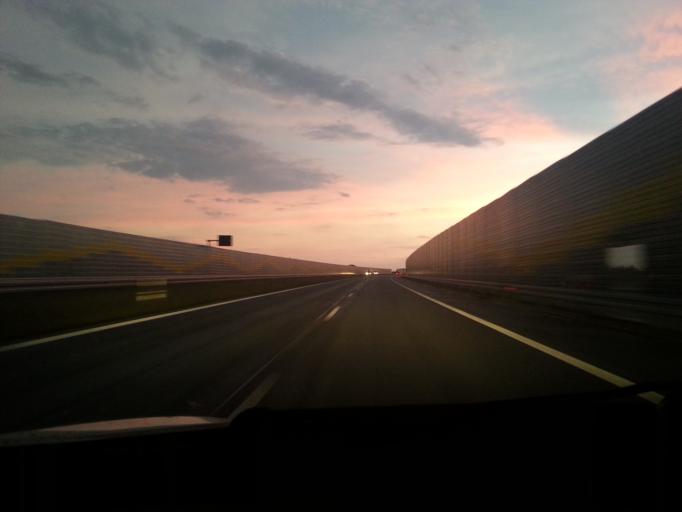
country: PL
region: Lodz Voivodeship
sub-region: Powiat zdunskowolski
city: Zdunska Wola
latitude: 51.5767
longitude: 18.9241
